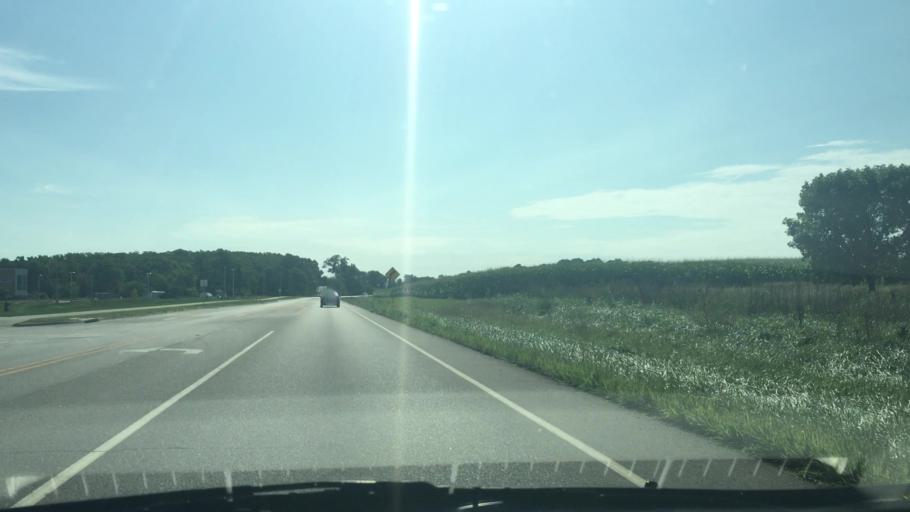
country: US
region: Iowa
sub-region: Johnson County
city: North Liberty
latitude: 41.7335
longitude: -91.5717
